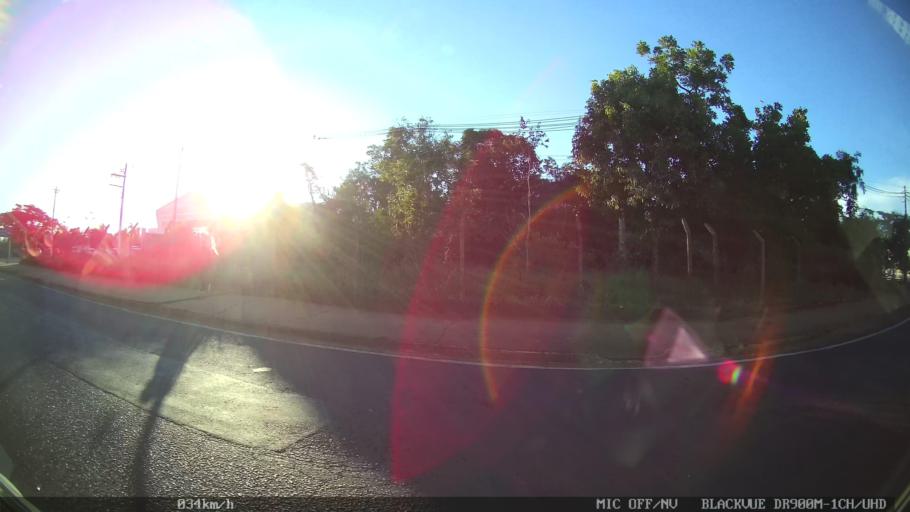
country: BR
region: Sao Paulo
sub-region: Araraquara
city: Araraquara
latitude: -21.7854
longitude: -48.2037
